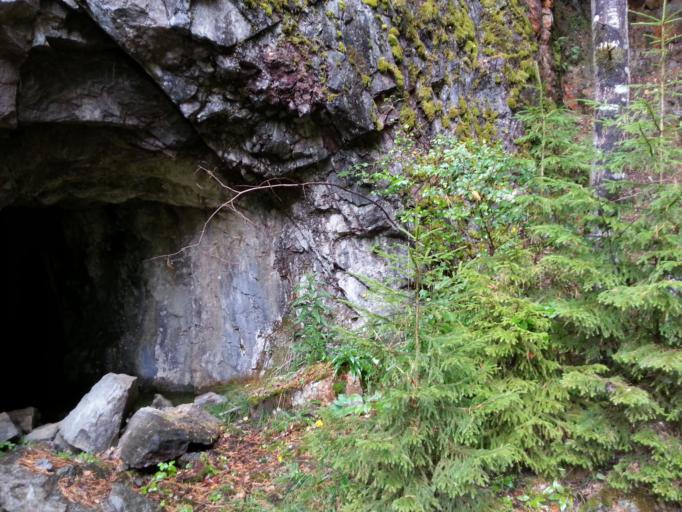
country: SE
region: OEstergoetland
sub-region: Finspangs Kommun
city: Finspang
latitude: 58.6347
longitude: 15.8240
